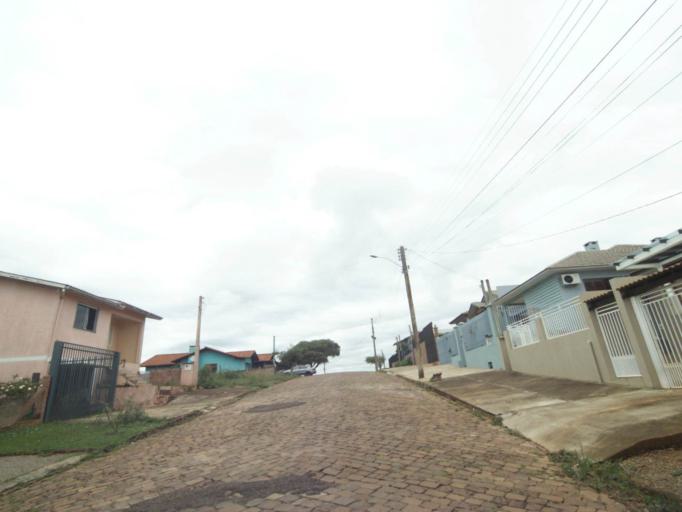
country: BR
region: Rio Grande do Sul
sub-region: Lagoa Vermelha
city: Lagoa Vermelha
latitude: -28.2169
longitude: -51.5311
